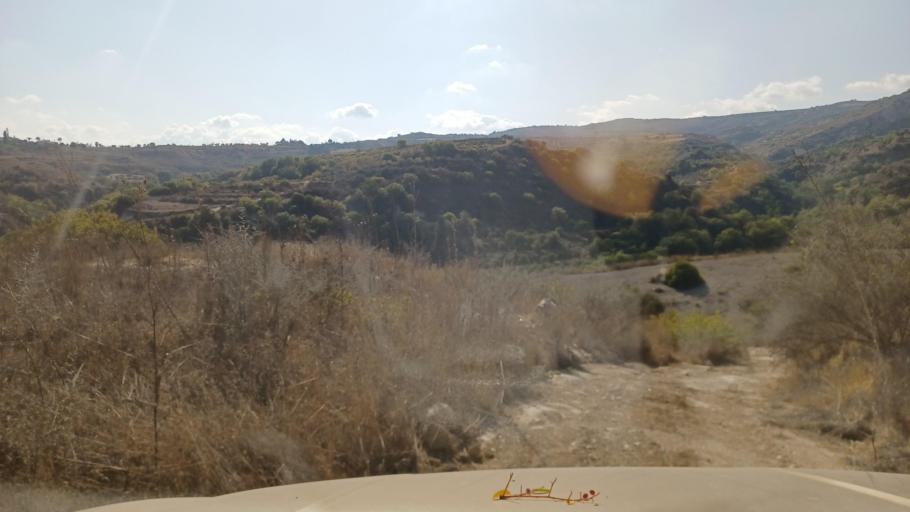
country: CY
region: Pafos
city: Pegeia
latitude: 34.9215
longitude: 32.4590
